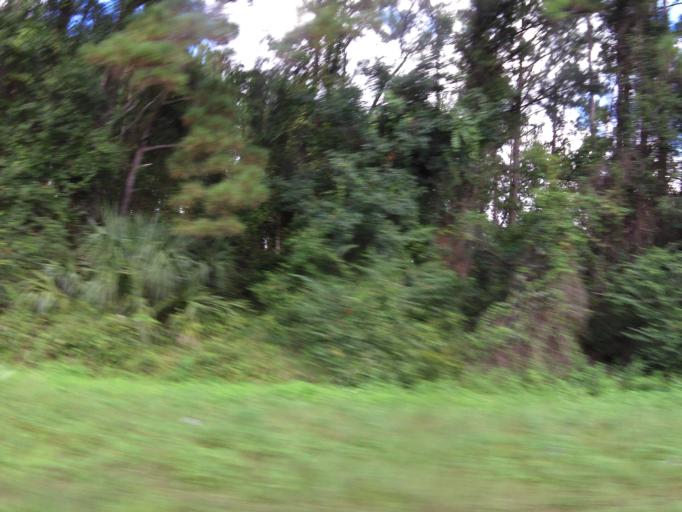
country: US
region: Georgia
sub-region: Camden County
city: Kingsland
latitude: 30.8232
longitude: -81.6948
